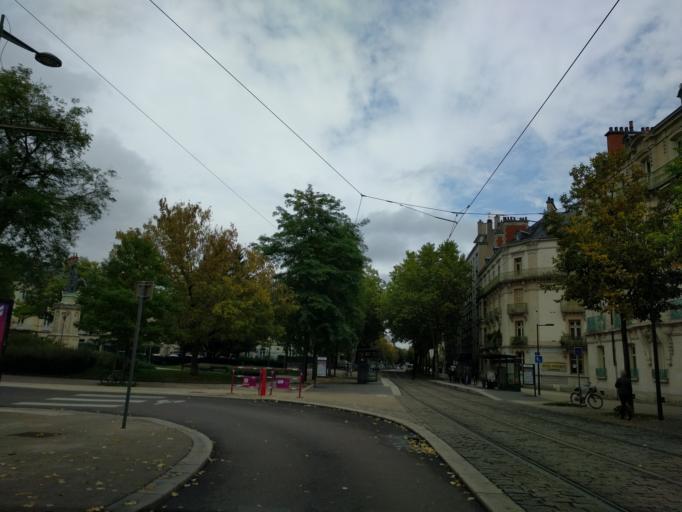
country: FR
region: Bourgogne
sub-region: Departement de la Cote-d'Or
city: Dijon
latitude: 47.3252
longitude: 5.0383
